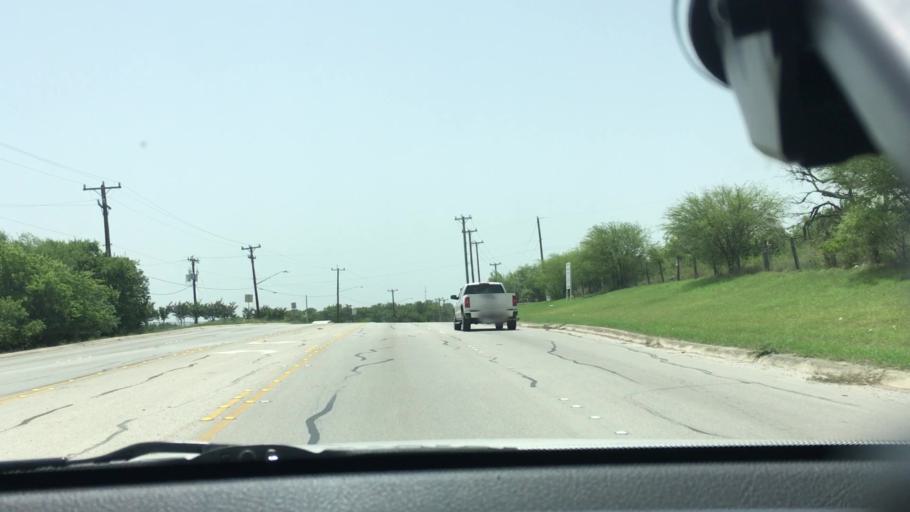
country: US
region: Texas
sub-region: Bexar County
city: Live Oak
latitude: 29.5652
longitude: -98.3533
